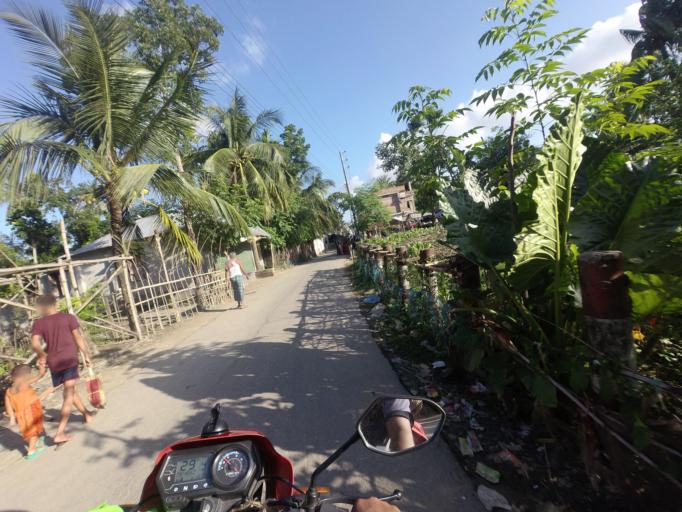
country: BD
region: Khulna
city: Khulna
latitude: 22.9208
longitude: 89.5178
